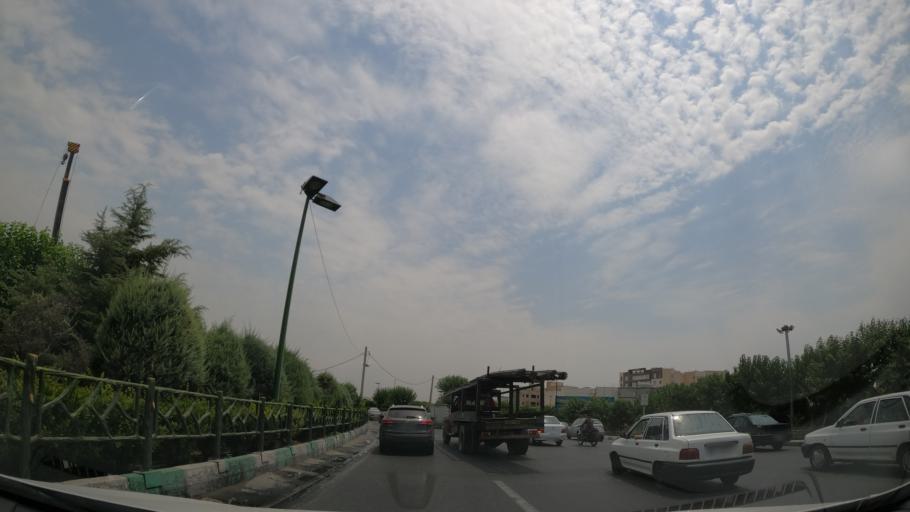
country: IR
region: Tehran
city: Tehran
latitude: 35.6786
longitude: 51.3401
